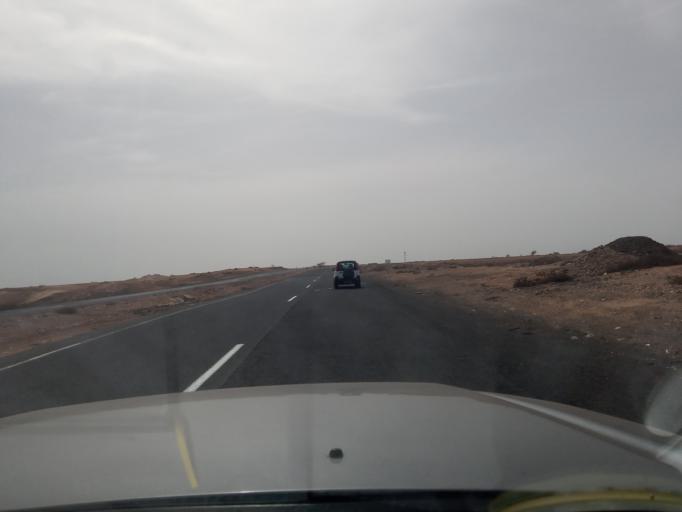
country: CV
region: Sal
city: Santa Maria
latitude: 16.6453
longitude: -22.9172
